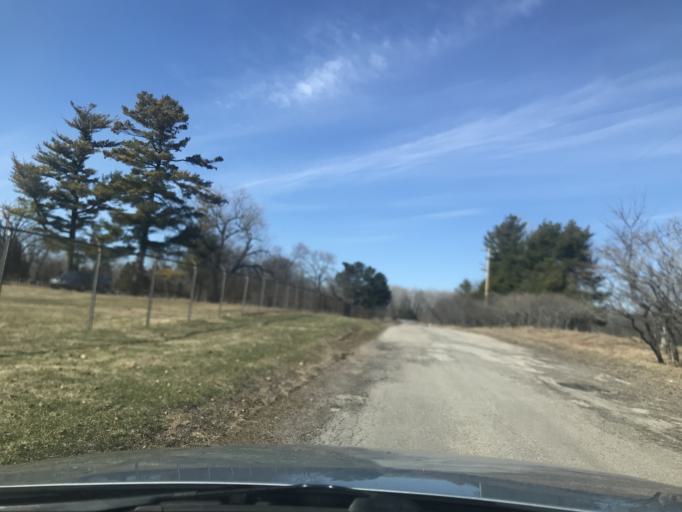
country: US
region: Wisconsin
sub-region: Marinette County
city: Marinette
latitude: 45.1125
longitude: -87.6510
